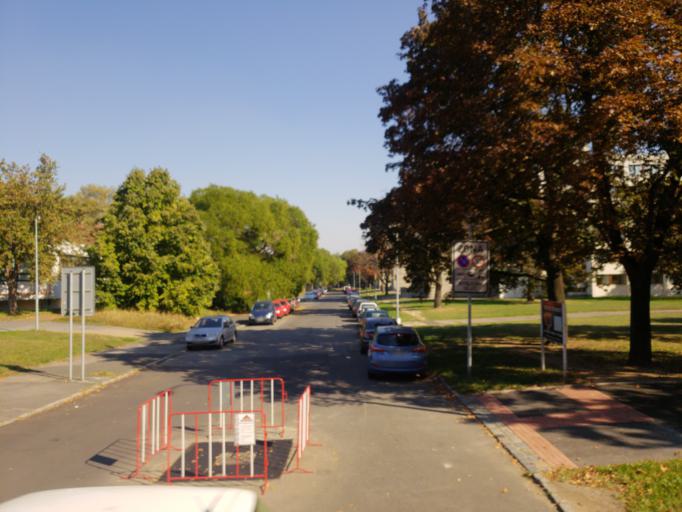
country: CZ
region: Praha
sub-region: Praha 1
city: Mala Strana
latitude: 50.0816
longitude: 14.3899
